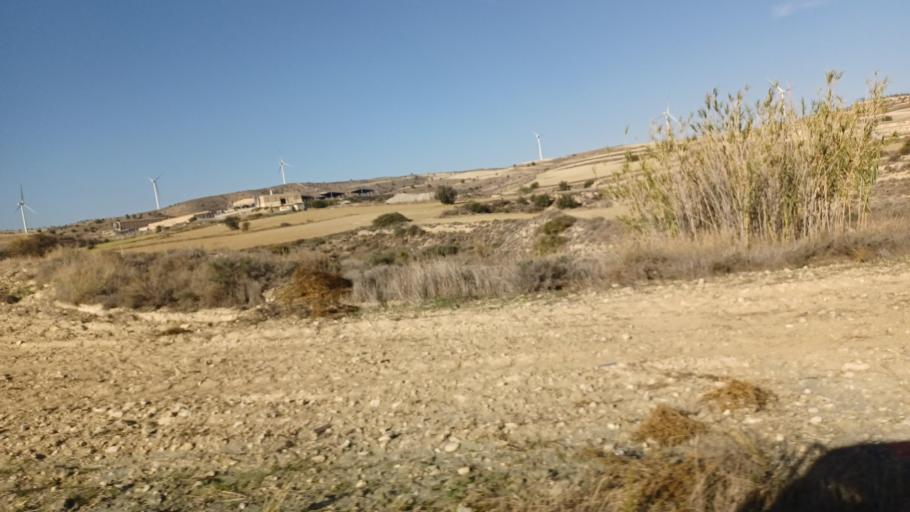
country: CY
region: Larnaka
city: Psevdas
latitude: 34.9657
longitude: 33.5137
